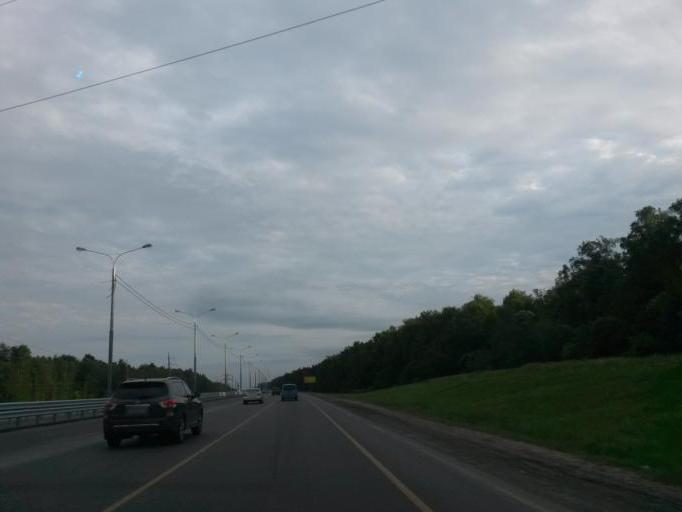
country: RU
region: Moskovskaya
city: L'vovskiy
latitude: 55.3033
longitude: 37.5482
